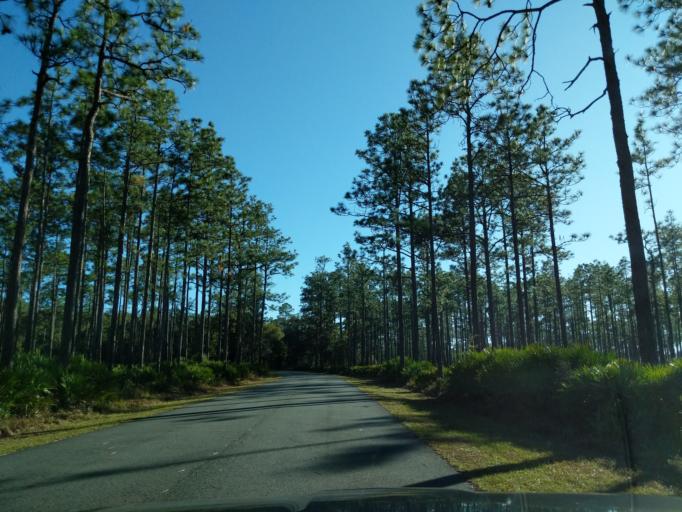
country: US
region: Georgia
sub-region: Charlton County
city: Folkston
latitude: 30.7324
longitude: -82.1362
